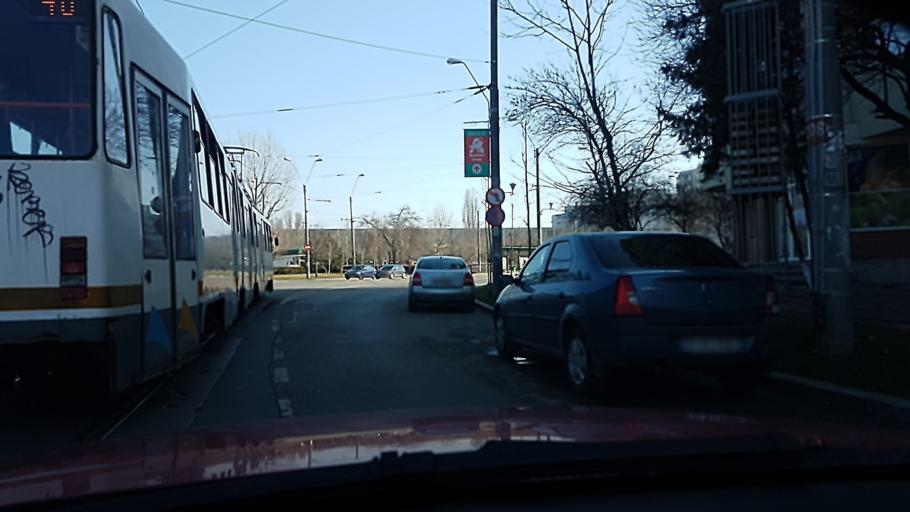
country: RO
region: Ilfov
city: Dobroesti
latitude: 44.4275
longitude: 26.1784
